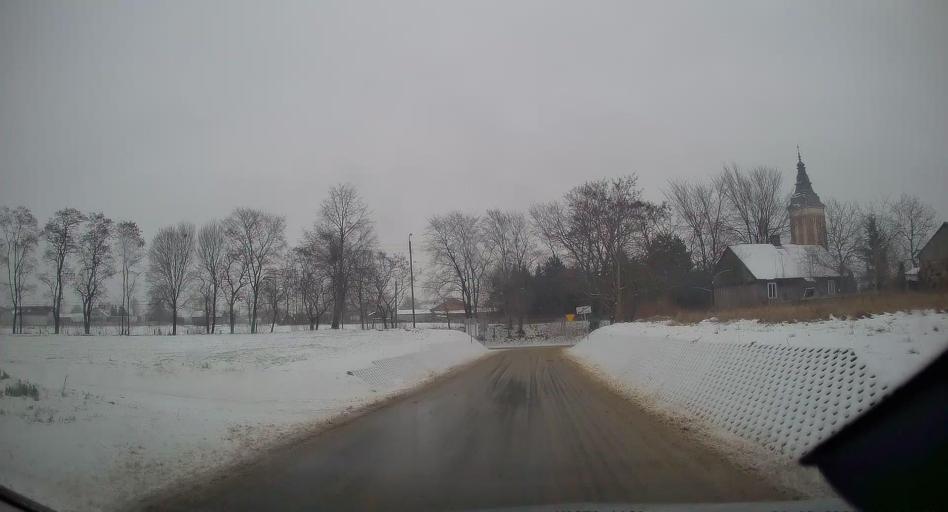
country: PL
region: Lodz Voivodeship
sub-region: Powiat tomaszowski
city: Czerniewice
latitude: 51.6777
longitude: 20.2183
